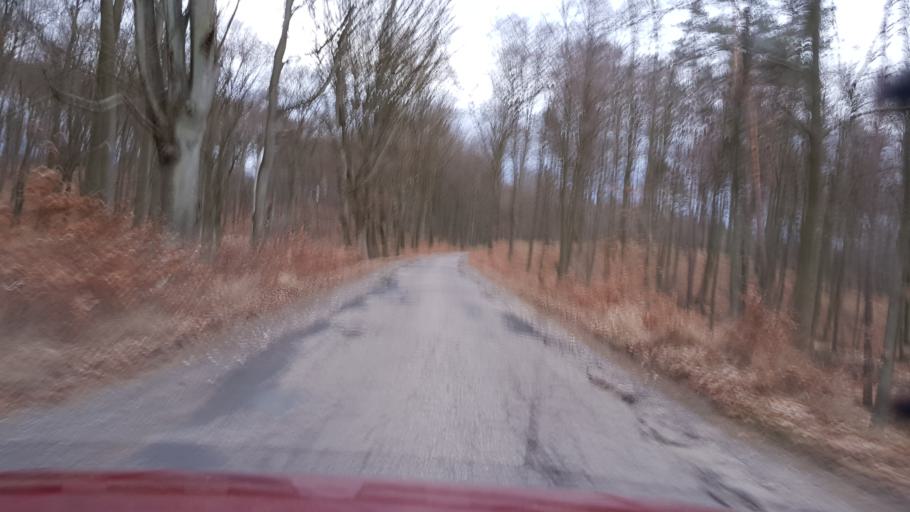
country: PL
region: West Pomeranian Voivodeship
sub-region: Szczecin
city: Szczecin
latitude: 53.3449
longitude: 14.6198
